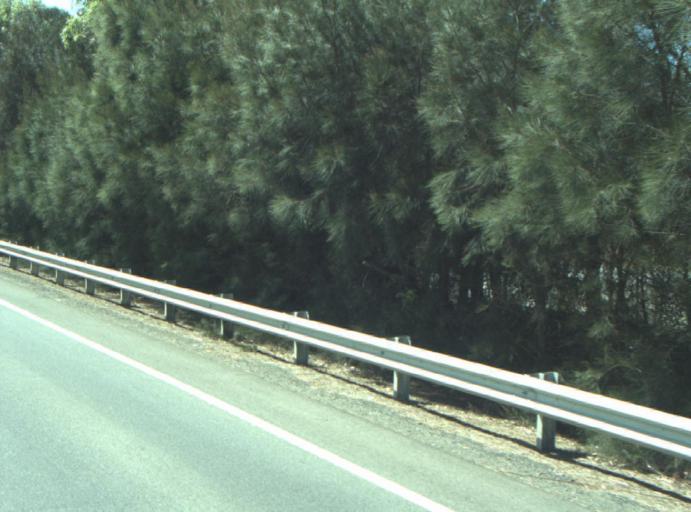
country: AU
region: Victoria
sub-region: Queenscliffe
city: Queenscliff
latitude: -38.1859
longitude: 144.6771
